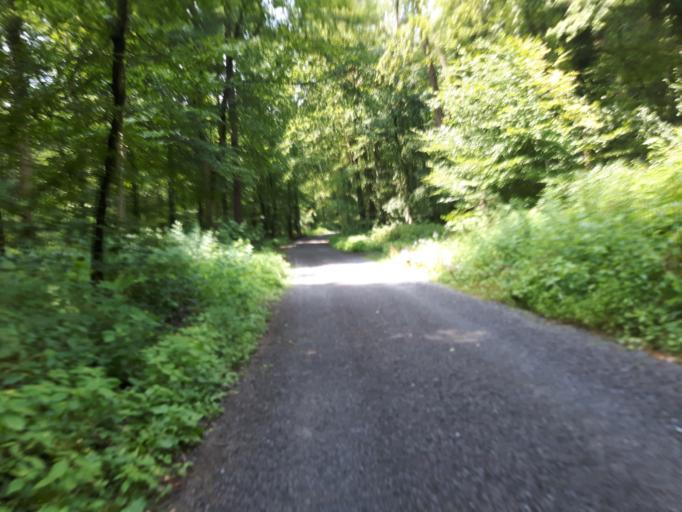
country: DE
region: Baden-Wuerttemberg
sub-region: Regierungsbezirk Stuttgart
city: Eppingen
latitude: 49.1275
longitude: 8.9372
